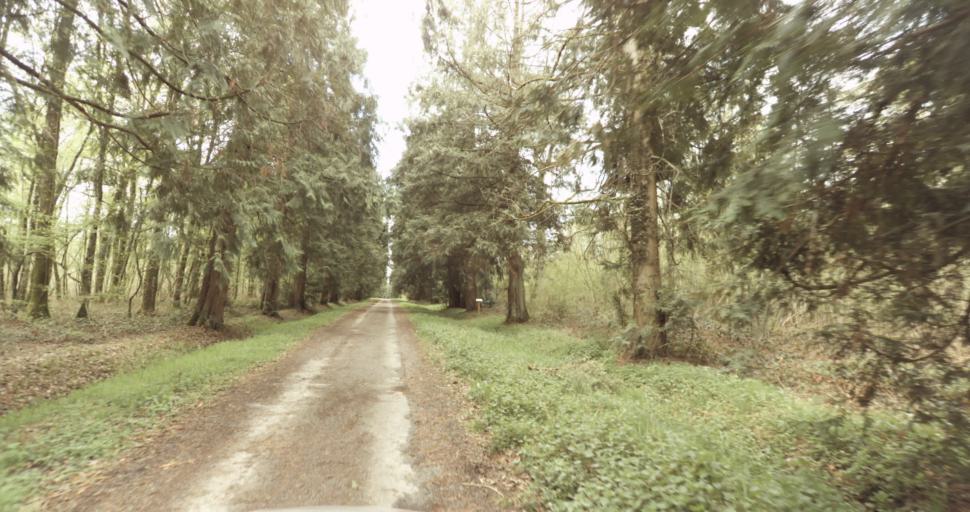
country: FR
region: Bourgogne
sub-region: Departement de la Cote-d'Or
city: Auxonne
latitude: 47.1714
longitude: 5.4276
